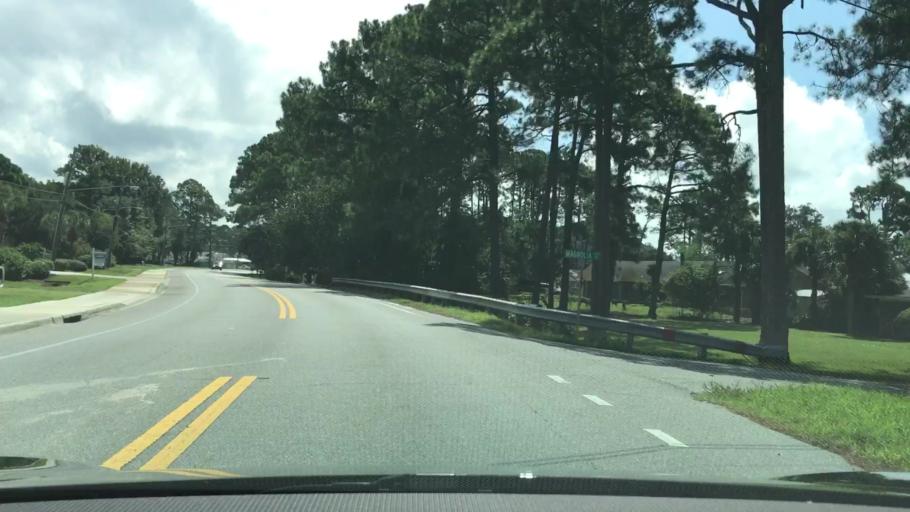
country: US
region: Florida
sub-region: Bay County
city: Lower Grand Lagoon
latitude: 30.1534
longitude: -85.7530
